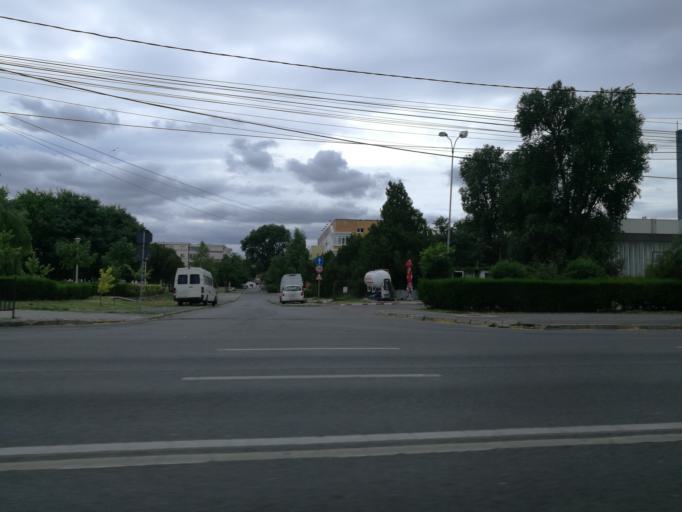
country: RO
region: Constanta
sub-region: Municipiul Constanta
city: Constanta
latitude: 44.1832
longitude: 28.6357
